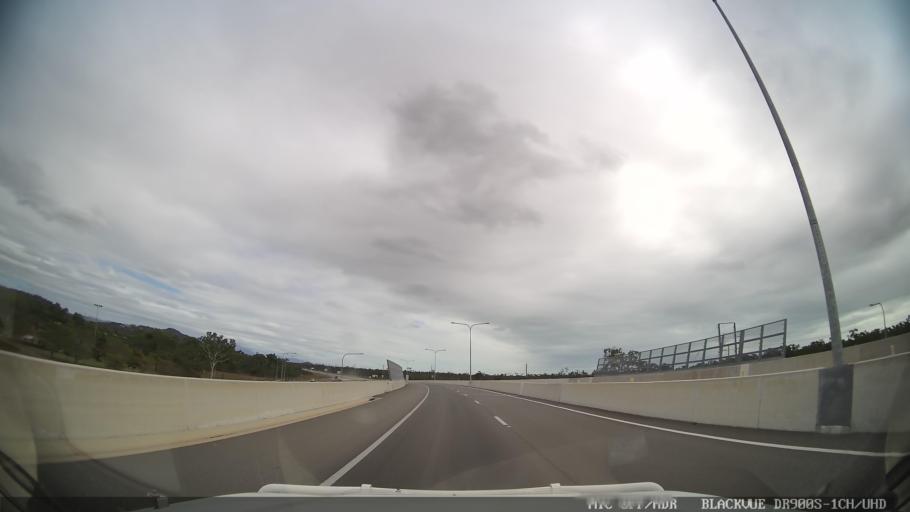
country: AU
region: Queensland
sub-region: Townsville
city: Bohle Plains
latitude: -19.2409
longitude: 146.6633
